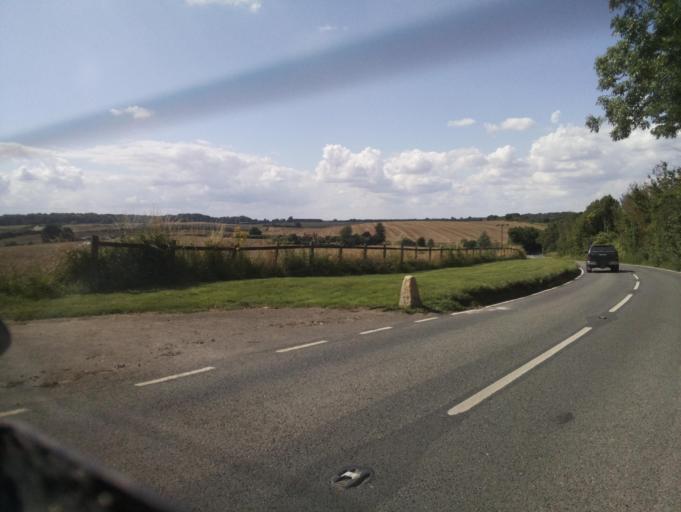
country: GB
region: England
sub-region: West Berkshire
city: Winterbourne
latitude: 51.4518
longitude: -1.3334
